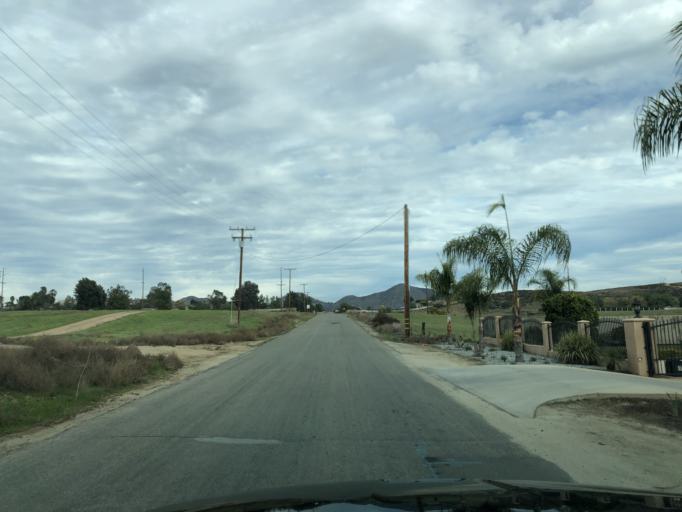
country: US
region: California
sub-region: Riverside County
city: Wildomar
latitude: 33.6086
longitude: -117.2851
